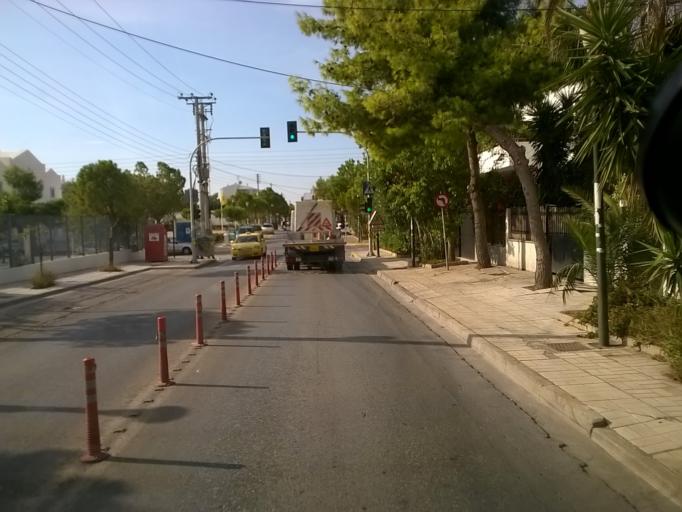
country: GR
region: Attica
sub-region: Nomarchia Athinas
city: Alimos
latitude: 37.9104
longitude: 23.7342
